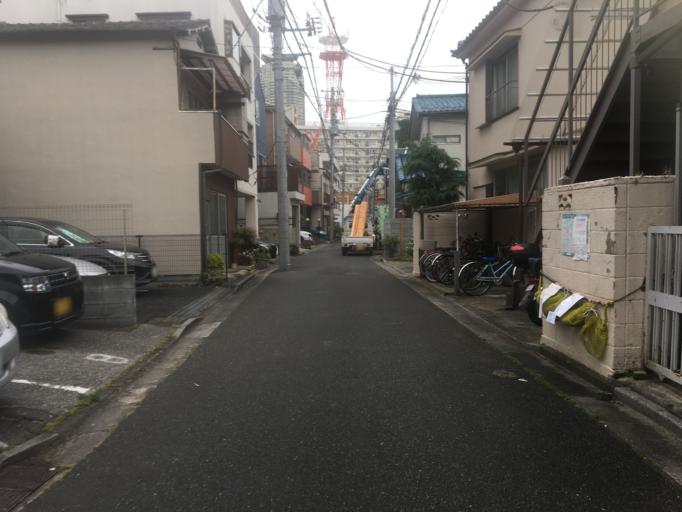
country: JP
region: Saitama
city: Kawaguchi
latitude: 35.7972
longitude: 139.7244
